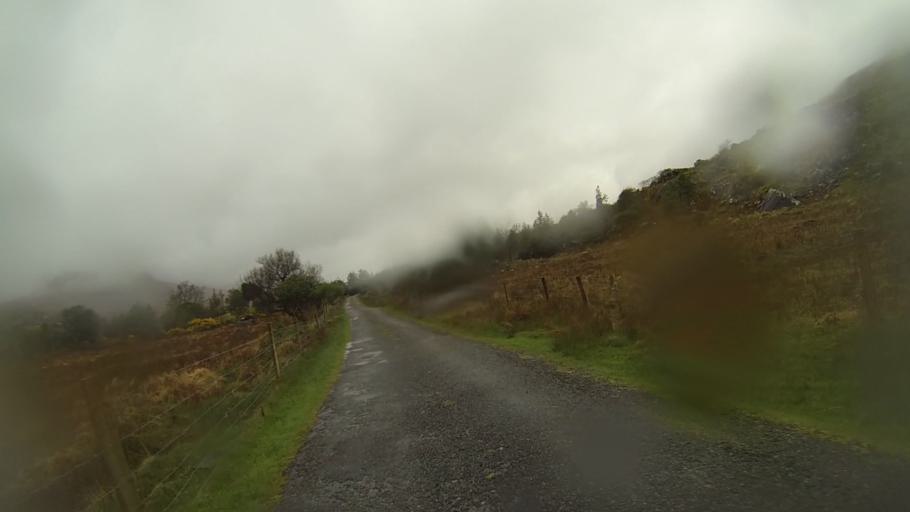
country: IE
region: Munster
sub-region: Ciarrai
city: Kenmare
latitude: 51.9490
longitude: -9.6681
